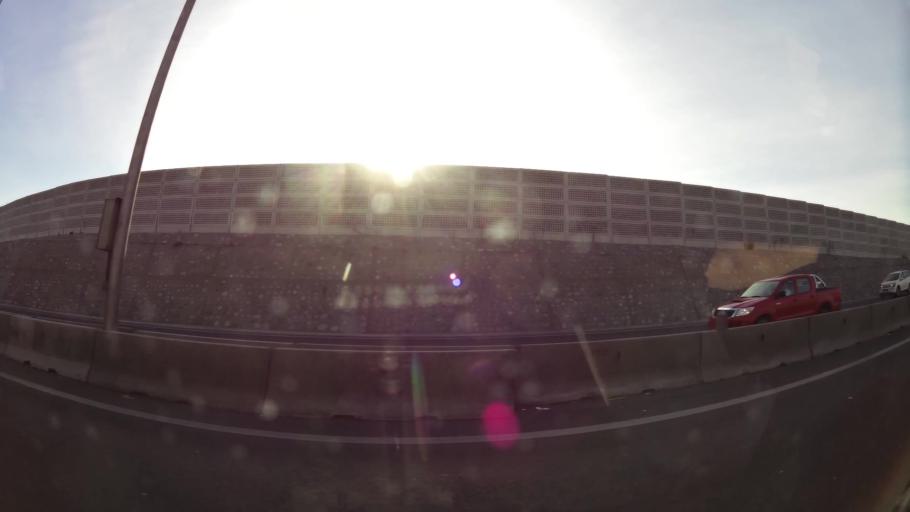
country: CL
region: Santiago Metropolitan
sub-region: Provincia de Santiago
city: La Pintana
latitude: -33.5657
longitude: -70.6135
